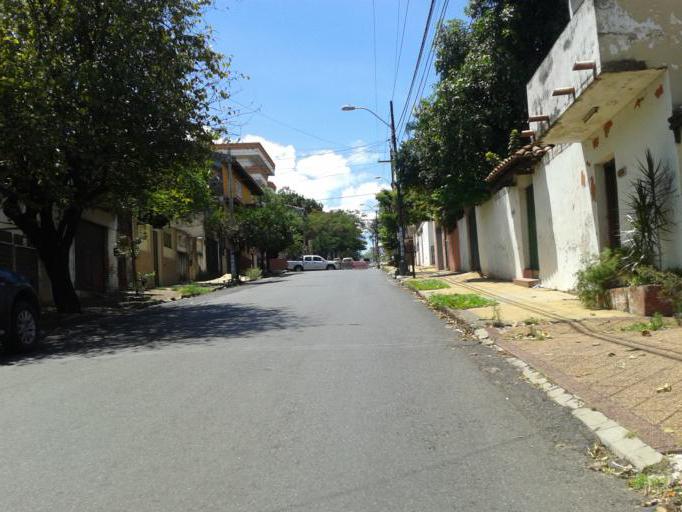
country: PY
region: Asuncion
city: Asuncion
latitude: -25.2945
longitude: -57.6197
